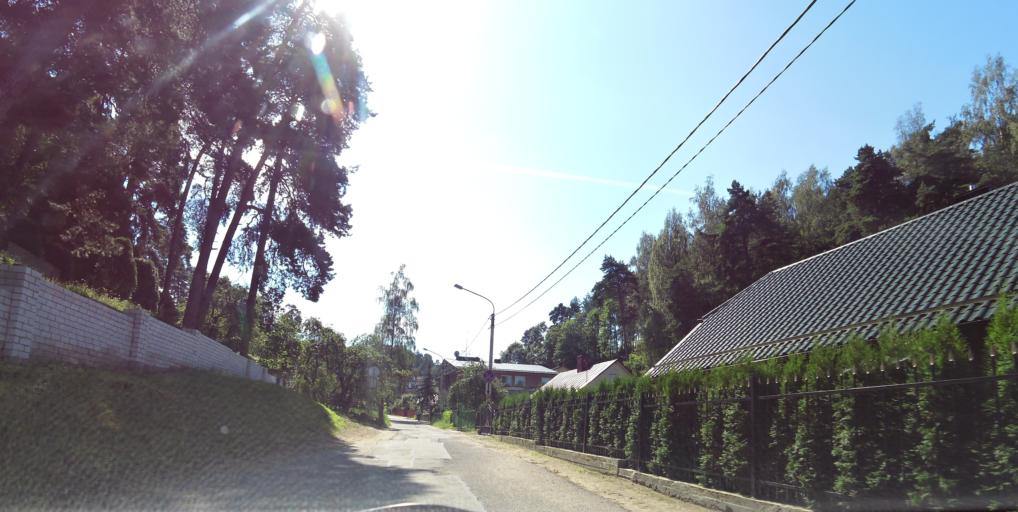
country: LT
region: Vilnius County
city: Rasos
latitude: 54.6939
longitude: 25.3113
